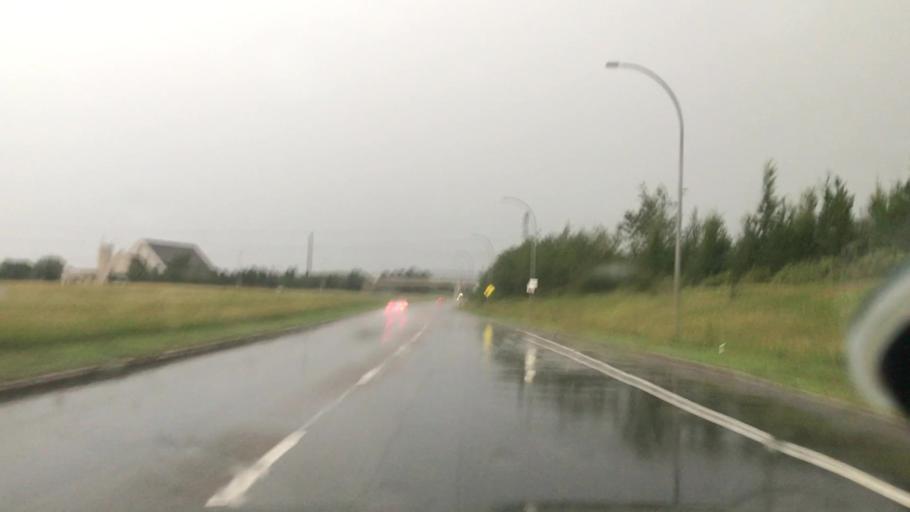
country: CA
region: Alberta
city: Edmonton
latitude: 53.4580
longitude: -113.5881
